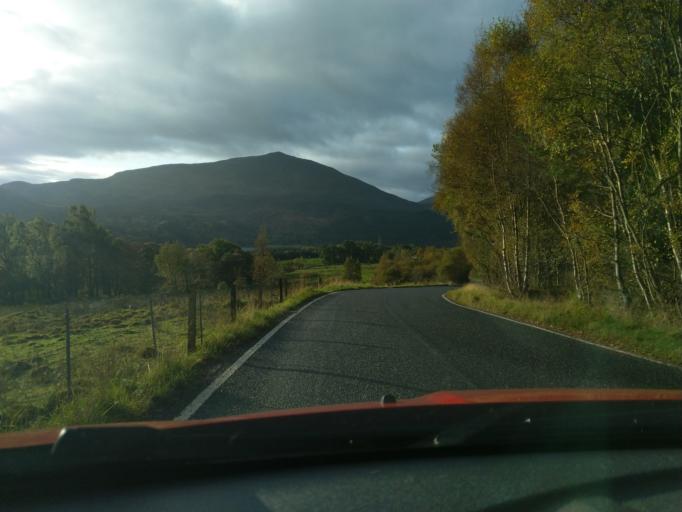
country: GB
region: Scotland
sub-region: Perth and Kinross
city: Aberfeldy
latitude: 56.7142
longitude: -4.1229
